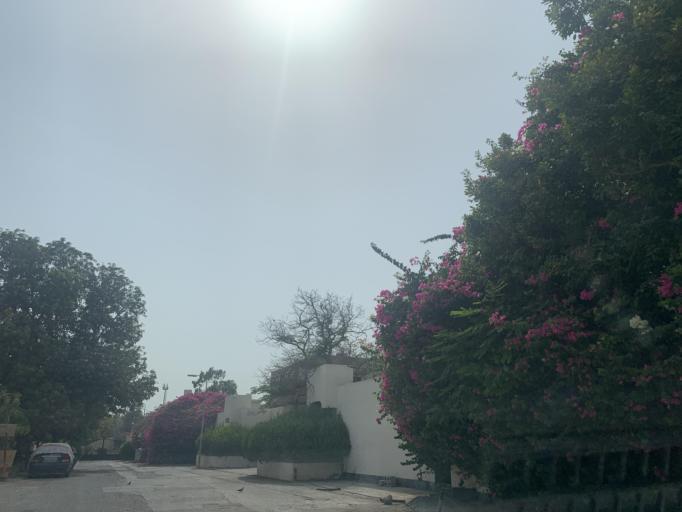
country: BH
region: Manama
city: Jidd Hafs
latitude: 26.2054
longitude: 50.4786
